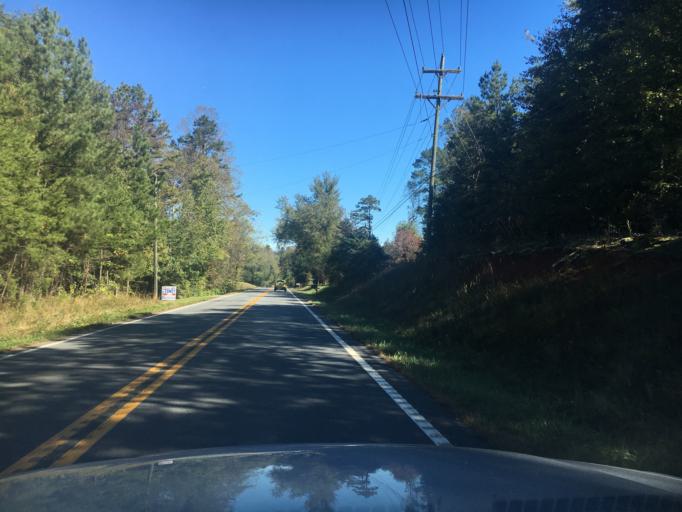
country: US
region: North Carolina
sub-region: Rutherford County
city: Spindale
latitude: 35.4233
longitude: -81.9057
